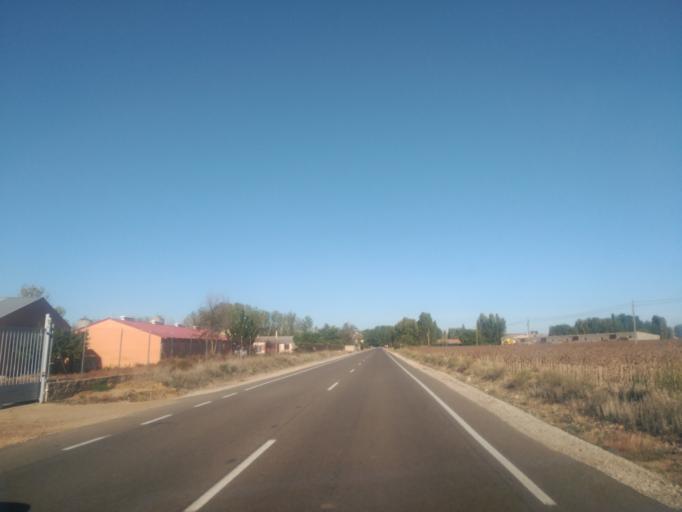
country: ES
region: Castille and Leon
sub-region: Provincia de Burgos
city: Zazuar
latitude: 41.6969
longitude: -3.5637
